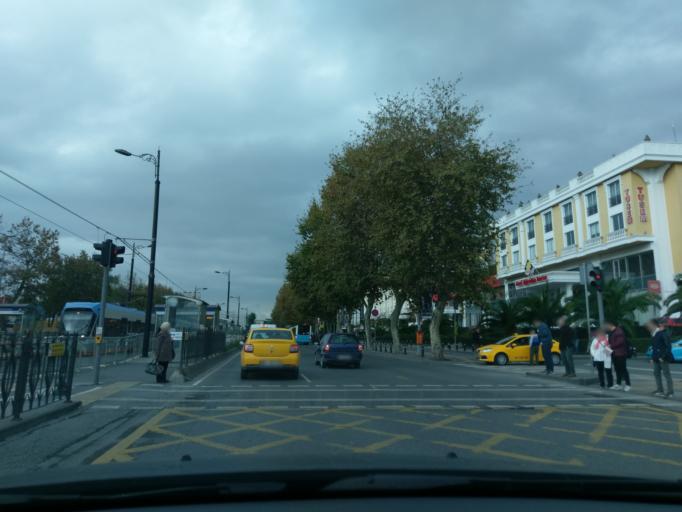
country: TR
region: Istanbul
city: Istanbul
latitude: 41.0181
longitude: 28.9277
